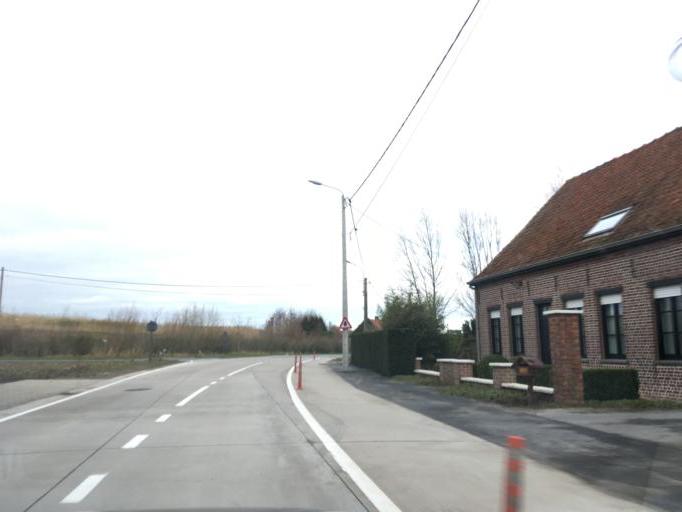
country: BE
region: Flanders
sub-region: Provincie West-Vlaanderen
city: Roeselare
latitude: 50.9130
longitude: 3.1397
